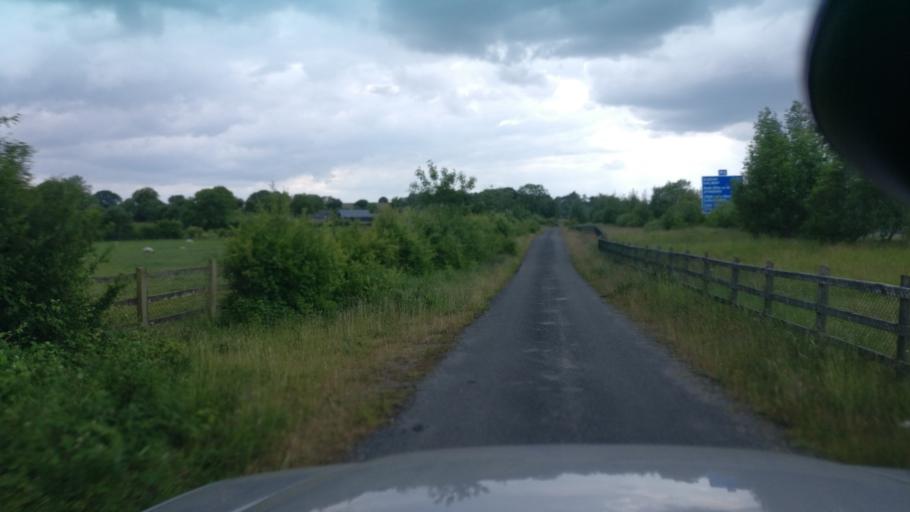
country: IE
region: Connaught
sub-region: County Galway
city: Ballinasloe
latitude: 53.3129
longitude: -8.2531
